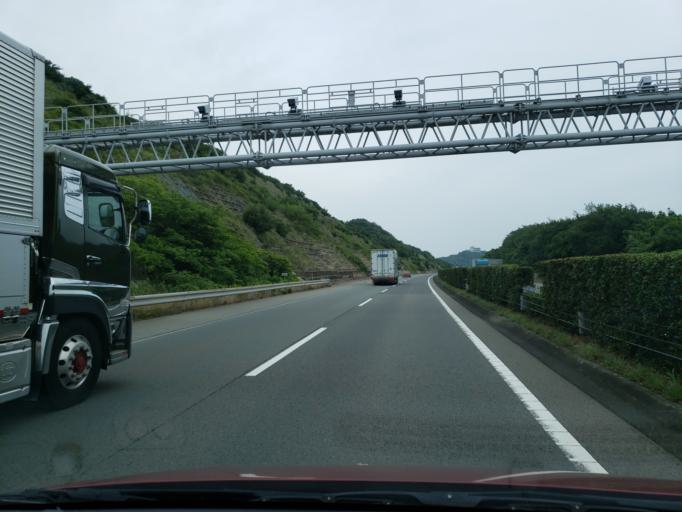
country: JP
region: Tokushima
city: Narutocho-mitsuishi
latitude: 34.2287
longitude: 134.6313
